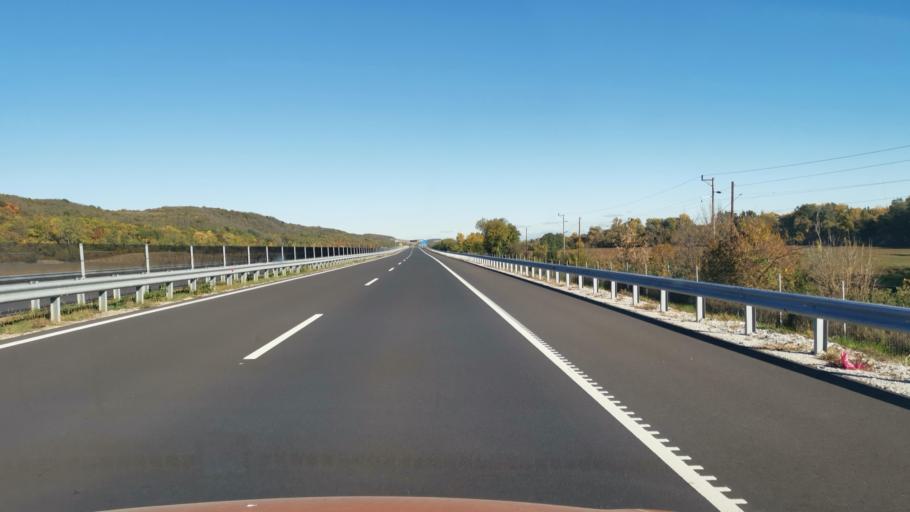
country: HU
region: Borsod-Abauj-Zemplen
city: Gonc
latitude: 48.4528
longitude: 21.1951
